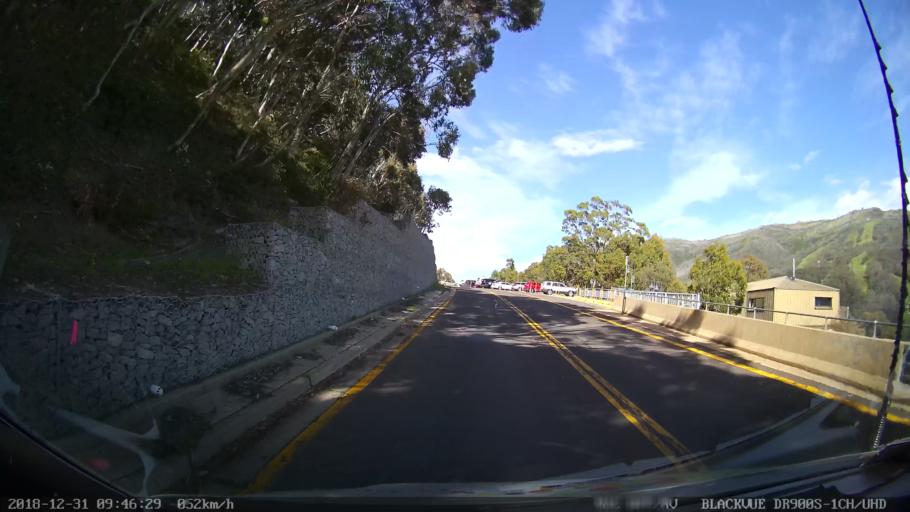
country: AU
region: New South Wales
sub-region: Snowy River
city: Jindabyne
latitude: -36.5040
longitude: 148.3089
